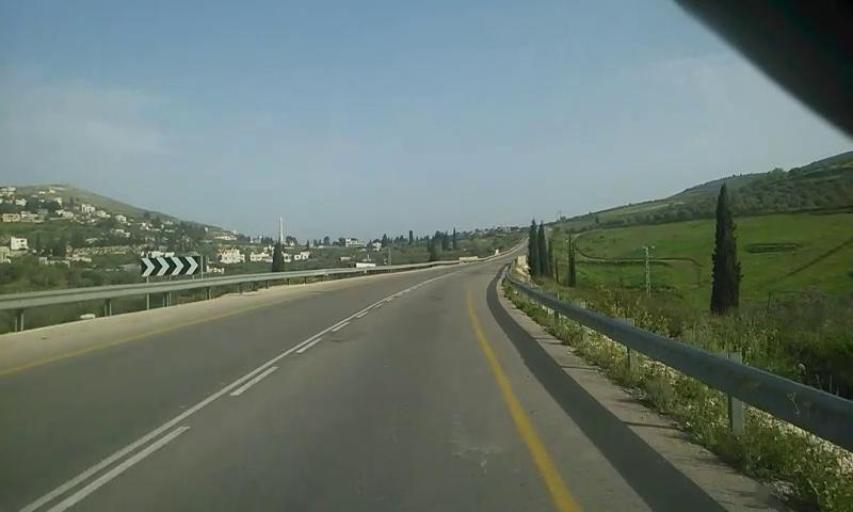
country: PS
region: West Bank
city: Burin
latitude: 32.1821
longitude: 35.2419
